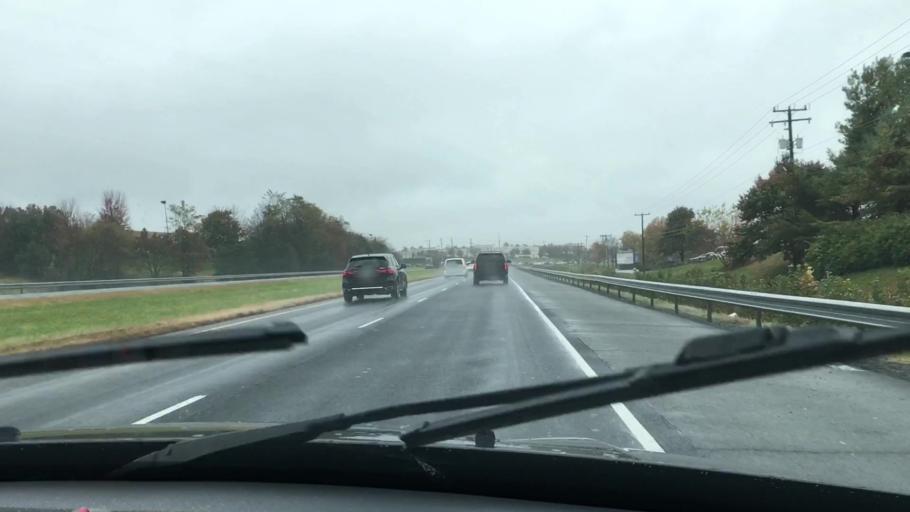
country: US
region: Virginia
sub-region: Loudoun County
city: Leesburg
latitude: 39.1176
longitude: -77.5393
